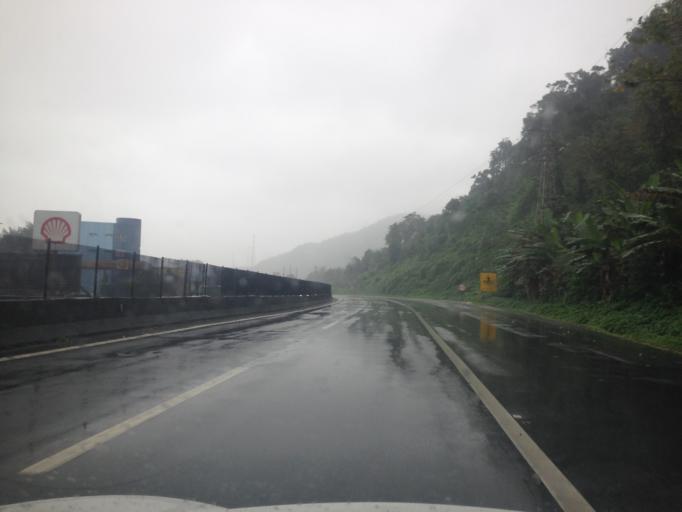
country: BR
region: Sao Paulo
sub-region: Mongagua
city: Mongagua
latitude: -24.0913
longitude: -46.6185
